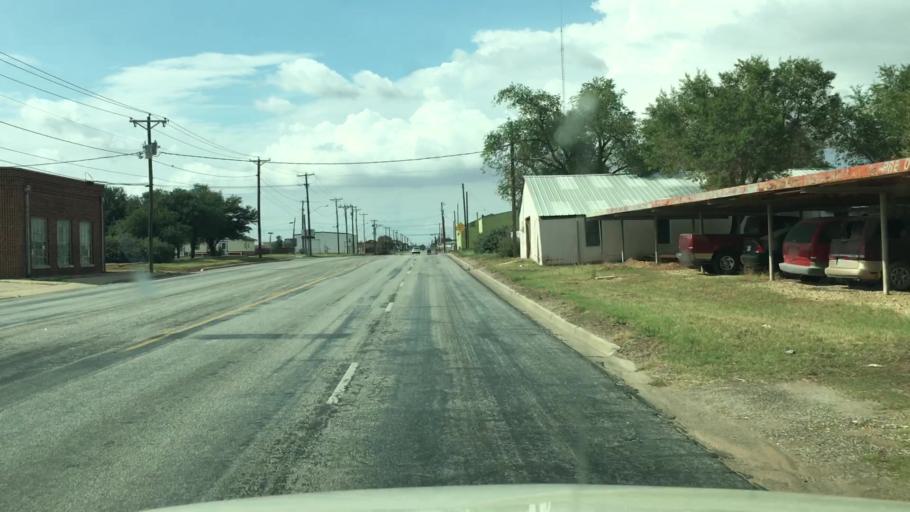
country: US
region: Texas
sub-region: Dawson County
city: Lamesa
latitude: 32.7308
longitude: -101.9483
